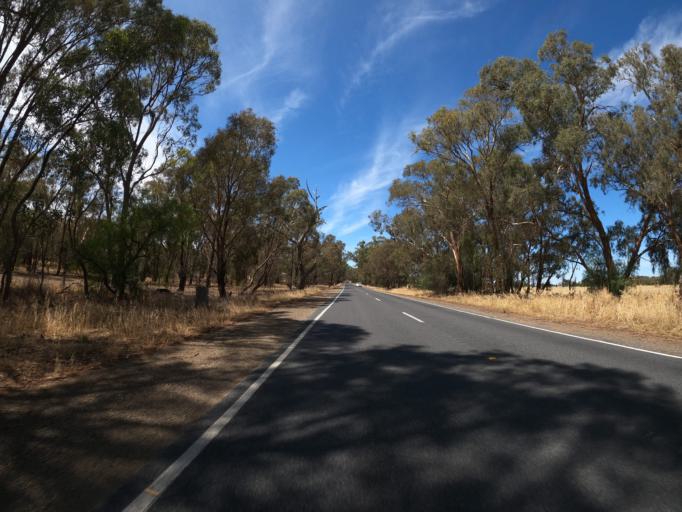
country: AU
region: Victoria
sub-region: Benalla
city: Benalla
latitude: -36.3920
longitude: 145.9803
